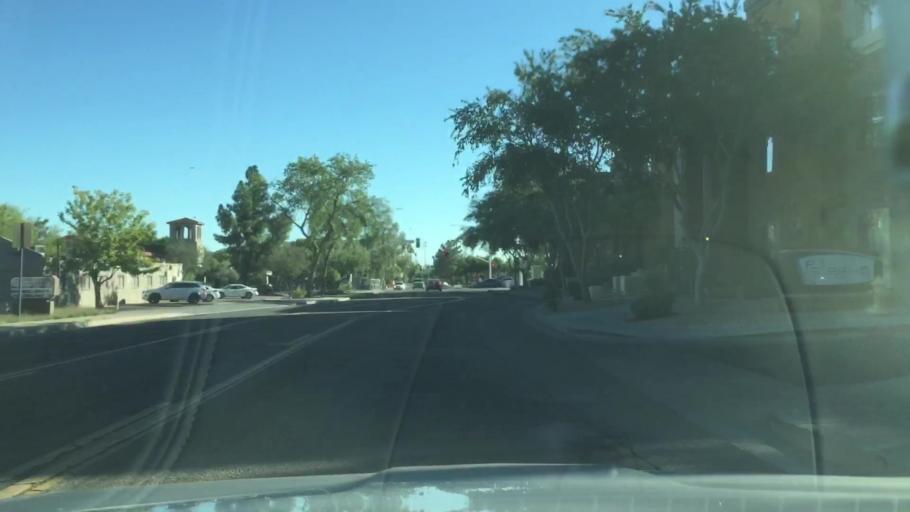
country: US
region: Arizona
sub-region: Maricopa County
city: Scottsdale
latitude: 33.4961
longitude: -111.9197
